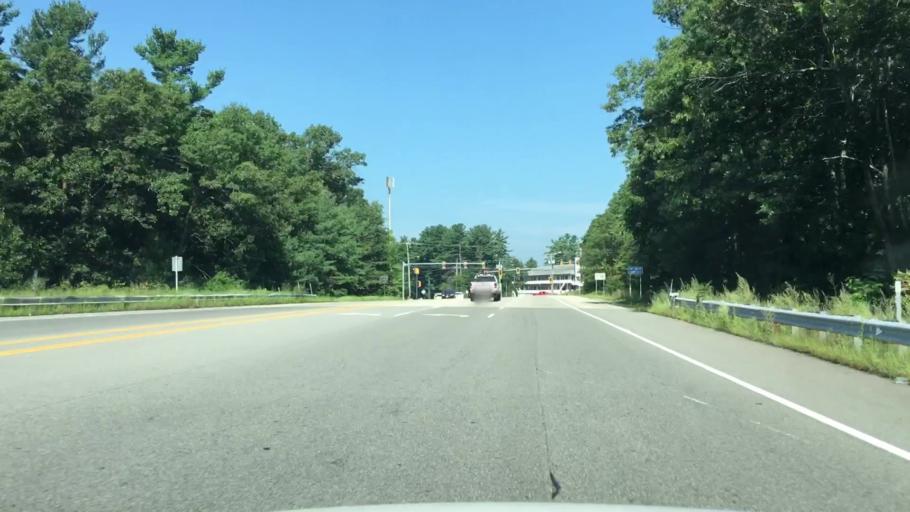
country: US
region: New Hampshire
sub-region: Rockingham County
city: Seabrook
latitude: 42.8957
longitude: -70.8841
